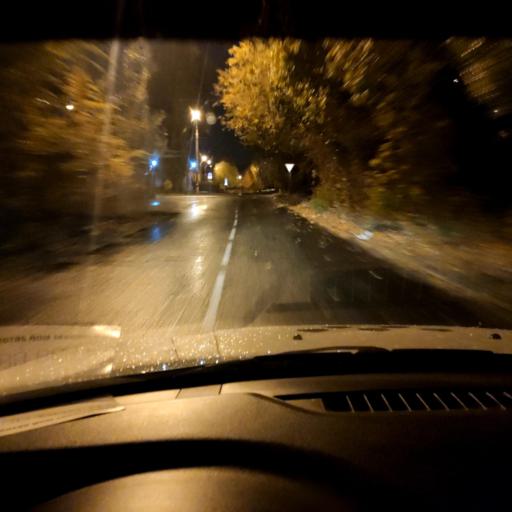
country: RU
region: Samara
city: Tol'yatti
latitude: 53.5160
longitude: 49.4010
